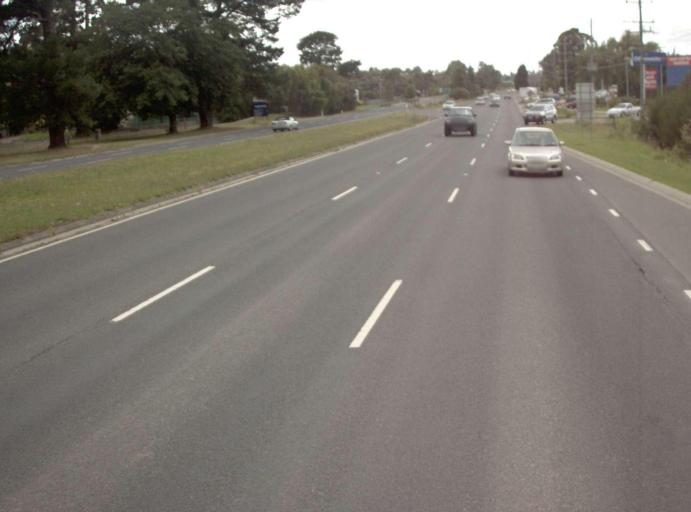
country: AU
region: Victoria
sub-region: Maroondah
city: Croydon North
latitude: -37.7685
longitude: 145.2988
